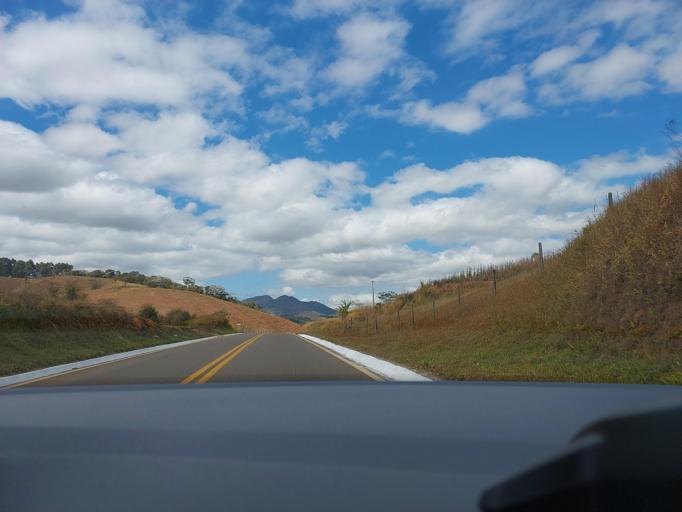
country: BR
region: Minas Gerais
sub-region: Visconde Do Rio Branco
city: Visconde do Rio Branco
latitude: -20.9241
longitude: -42.6367
